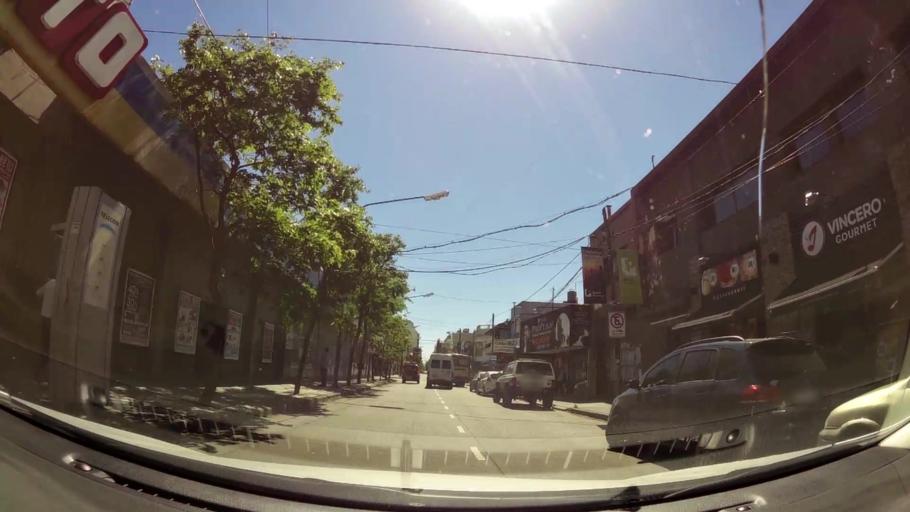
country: AR
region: Buenos Aires
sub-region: Partido de Vicente Lopez
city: Olivos
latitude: -34.5331
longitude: -58.5024
